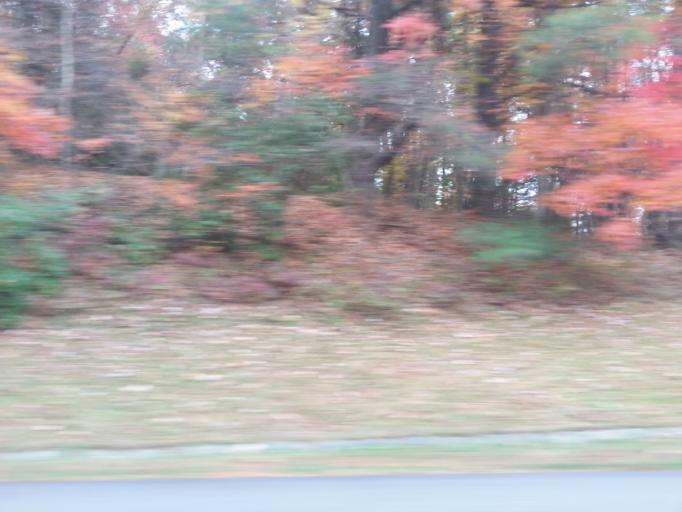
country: US
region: North Carolina
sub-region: Ashe County
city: Jefferson
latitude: 36.3138
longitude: -81.3635
